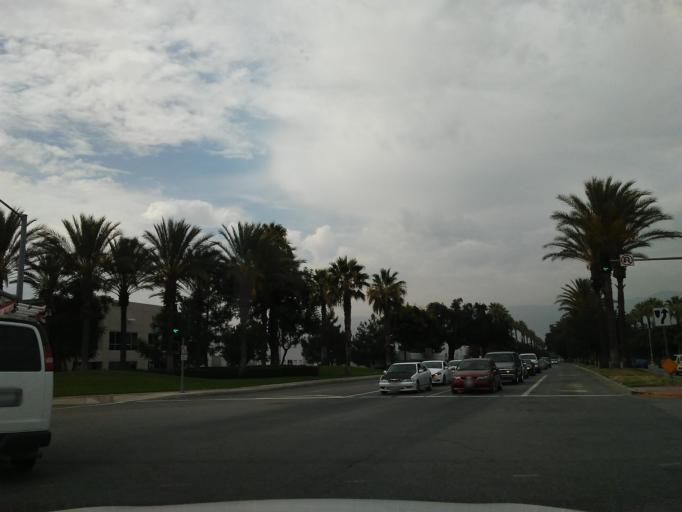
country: US
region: California
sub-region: San Bernardino County
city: San Bernardino
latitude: 34.0921
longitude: -117.2597
